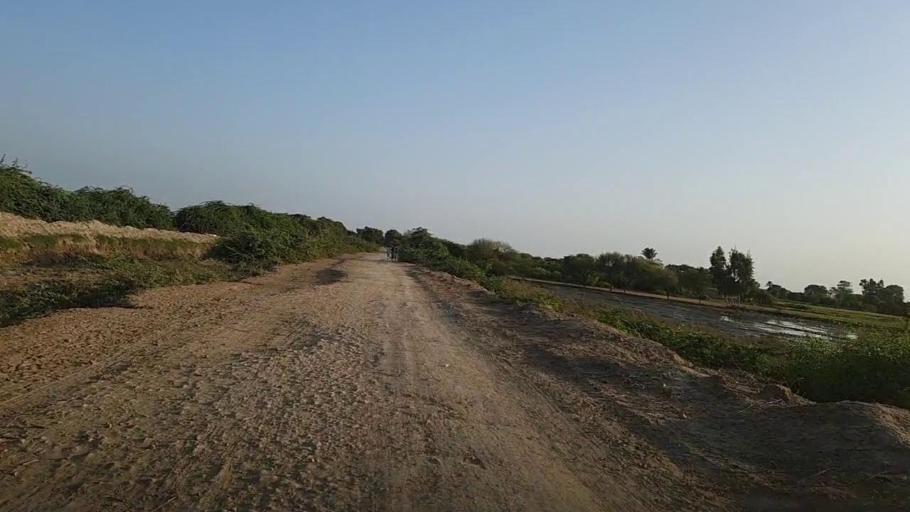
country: PK
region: Sindh
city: Kario
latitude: 24.7020
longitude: 68.6700
